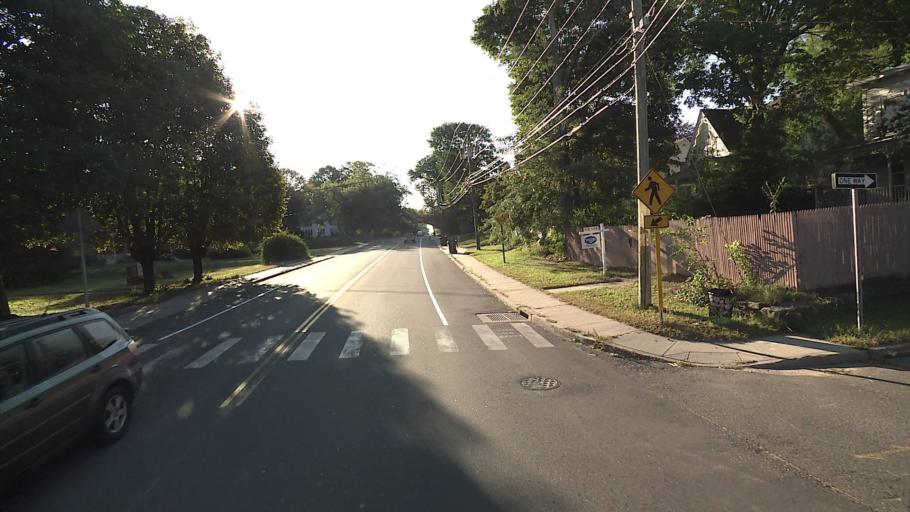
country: US
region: Connecticut
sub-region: Windham County
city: Willimantic
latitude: 41.7087
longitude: -72.2054
